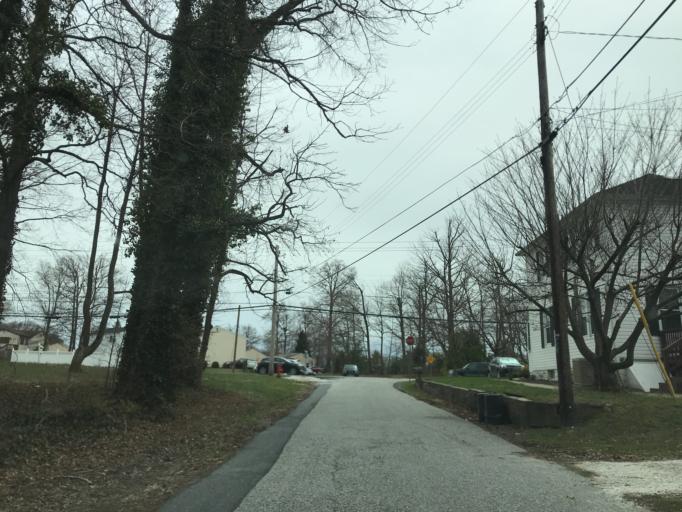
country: US
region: Maryland
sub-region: Baltimore County
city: Middle River
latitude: 39.2953
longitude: -76.4186
